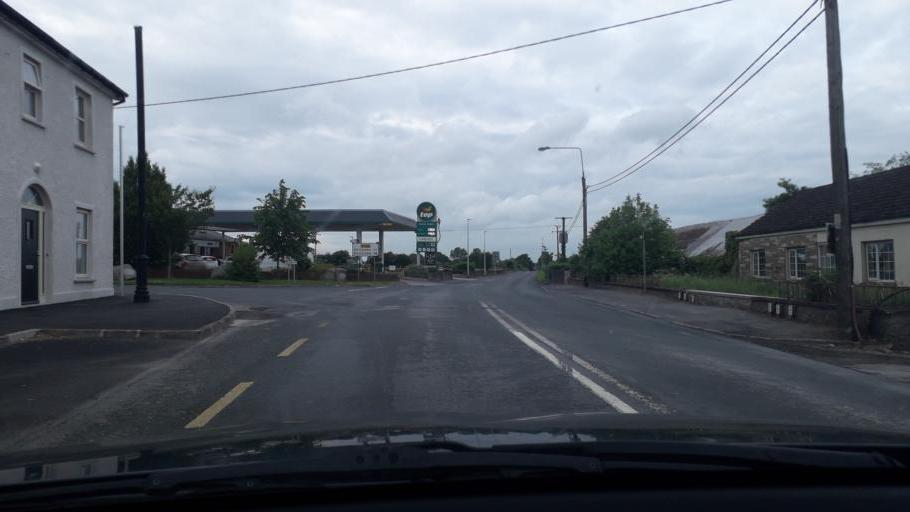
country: IE
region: Leinster
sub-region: Kildare
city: Castledermot
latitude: 52.9153
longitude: -6.8373
